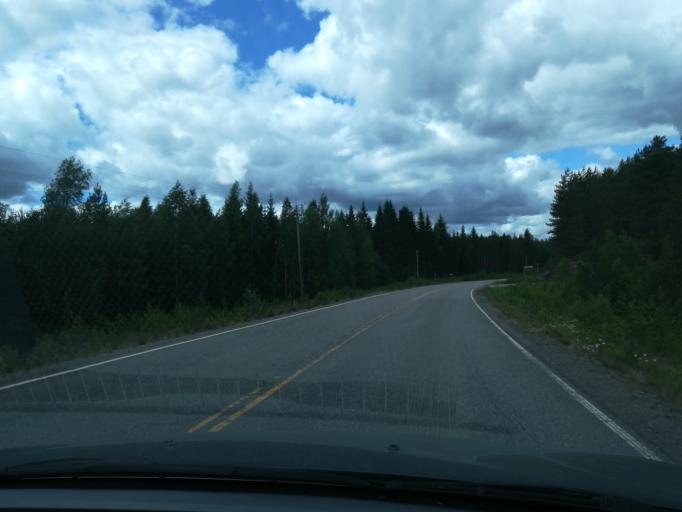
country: FI
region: Southern Savonia
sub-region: Mikkeli
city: Maentyharju
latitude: 61.3637
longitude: 27.0065
